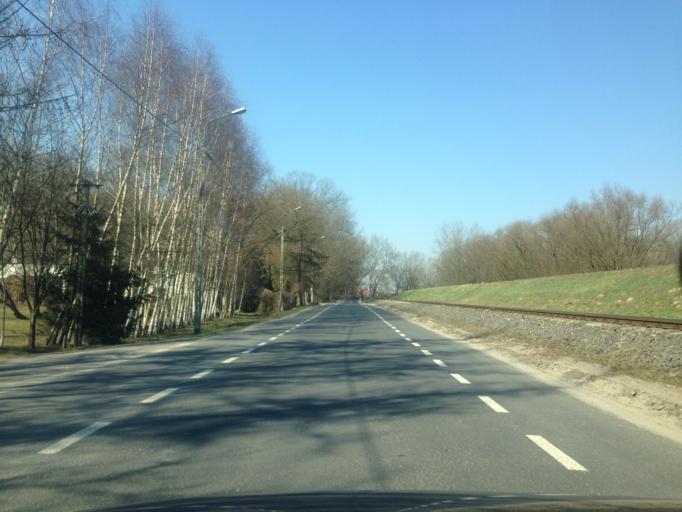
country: PL
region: Masovian Voivodeship
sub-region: Warszawa
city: Wilanow
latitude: 52.1663
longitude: 21.1267
